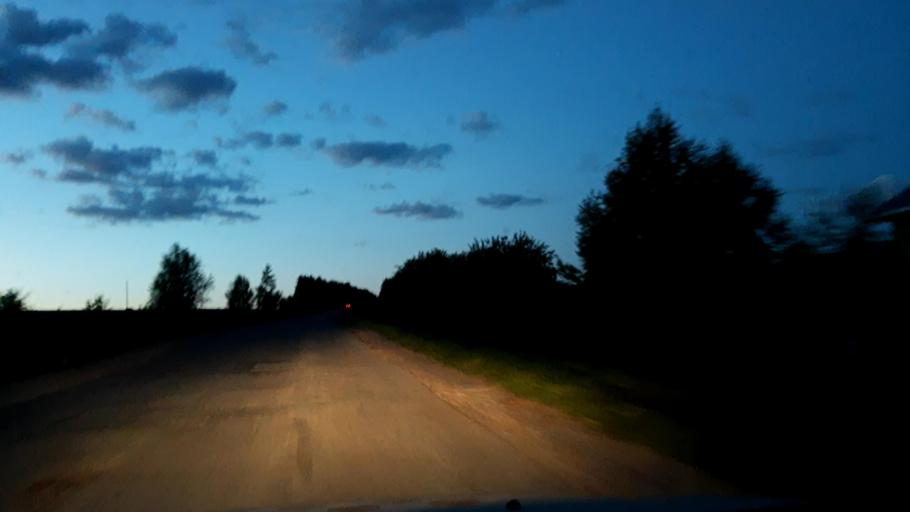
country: RU
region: Nizjnij Novgorod
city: Pamyat' Parizhskoy Kommuny
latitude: 56.0486
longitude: 44.4374
